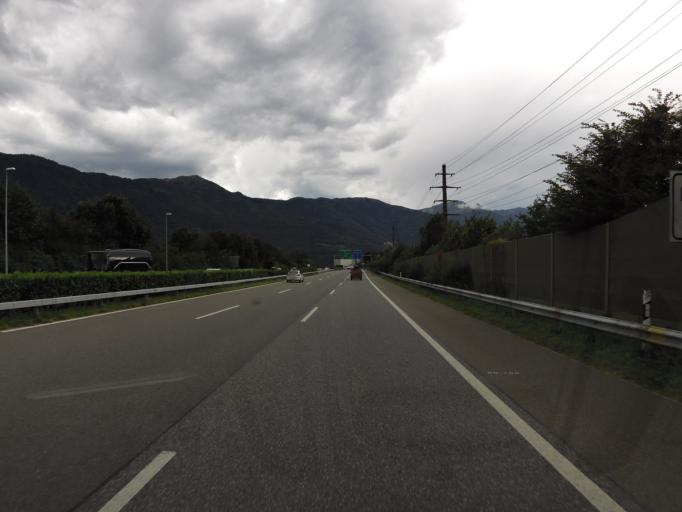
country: CH
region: Ticino
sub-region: Bellinzona District
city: Monte Carasso
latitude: 46.1797
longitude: 8.9984
